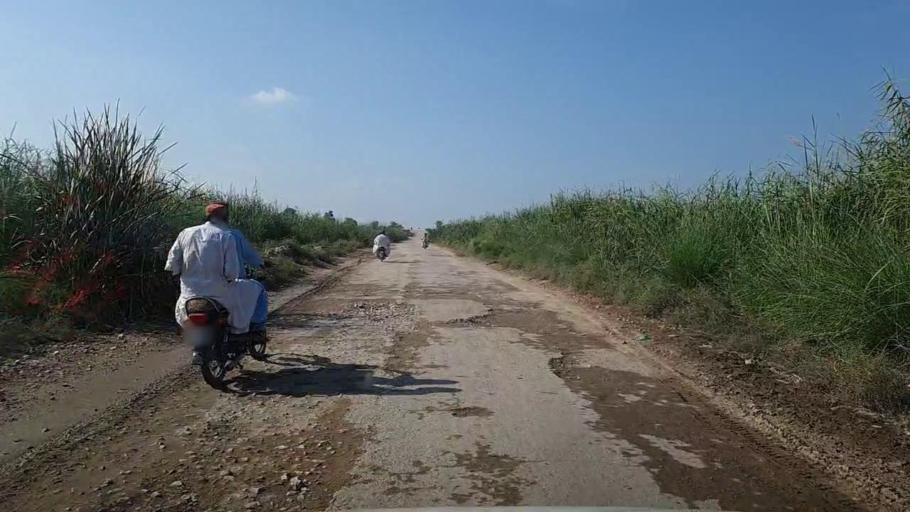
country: PK
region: Sindh
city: Kandiaro
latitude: 27.0693
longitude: 68.3144
